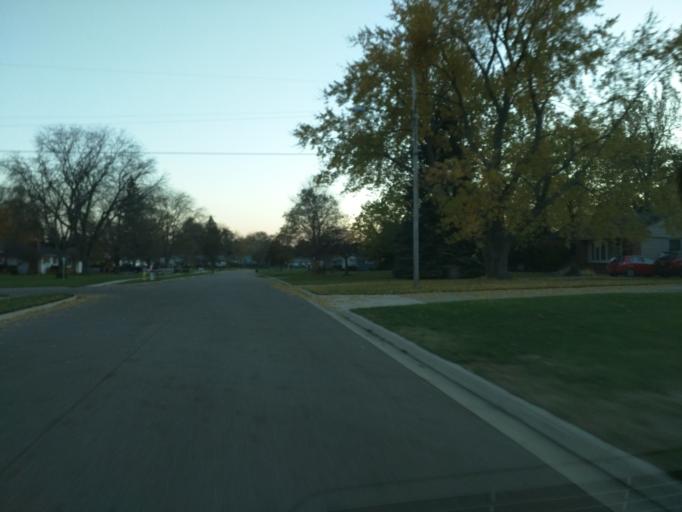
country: US
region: Michigan
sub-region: Eaton County
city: Waverly
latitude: 42.7294
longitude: -84.6086
